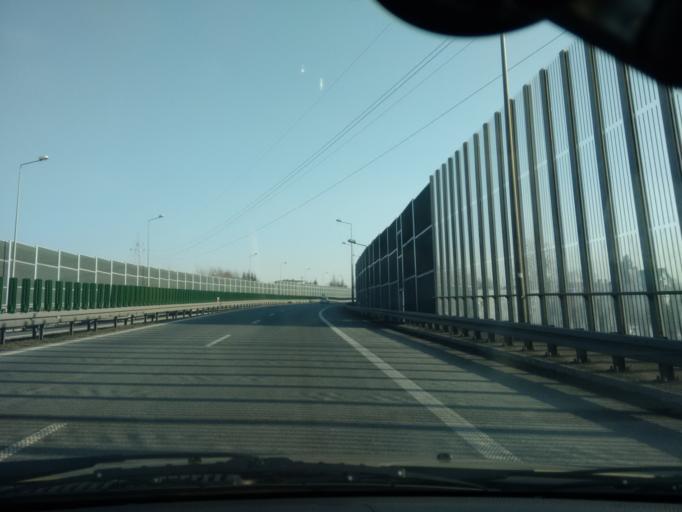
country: PL
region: Silesian Voivodeship
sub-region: Bielsko-Biala
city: Bielsko-Biala
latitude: 49.8491
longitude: 19.0536
